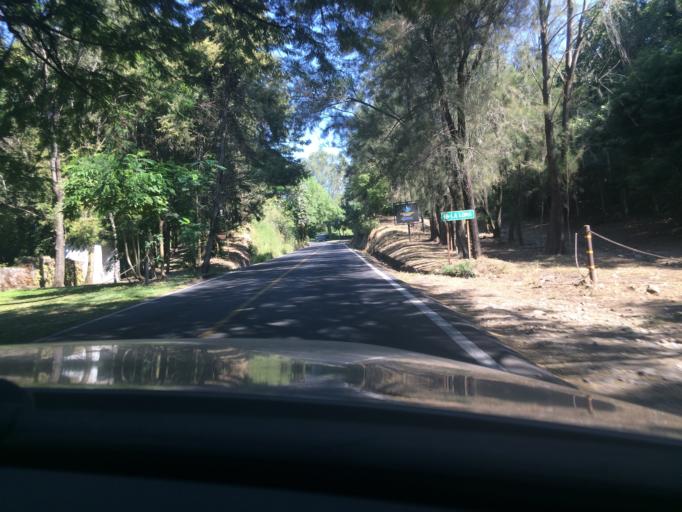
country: MX
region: Colima
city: Suchitlan
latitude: 19.3689
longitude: -103.7223
